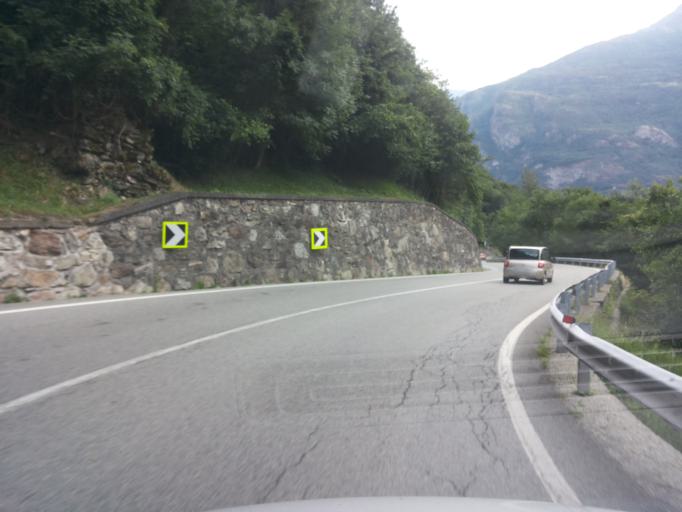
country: IT
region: Aosta Valley
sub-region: Valle d'Aosta
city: Perloz
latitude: 45.6038
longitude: 7.8071
